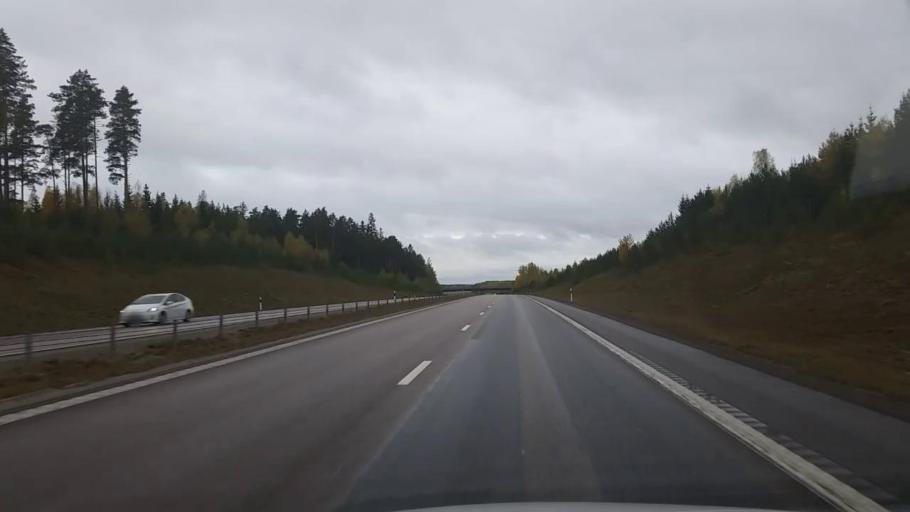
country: SE
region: Uppsala
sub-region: Osthammars Kommun
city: Bjorklinge
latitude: 60.1334
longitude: 17.5474
